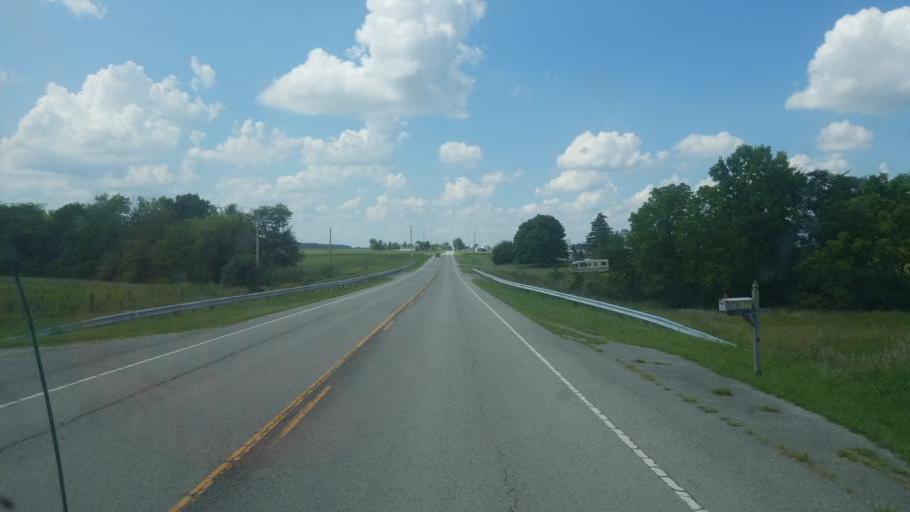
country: US
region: Ohio
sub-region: Hancock County
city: Arlington
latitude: 40.8341
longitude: -83.7046
